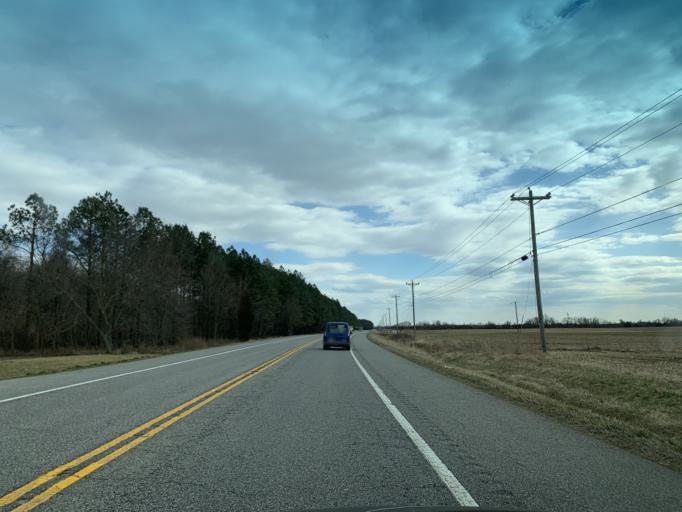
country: US
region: Maryland
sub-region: Queen Anne's County
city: Centreville
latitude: 38.9868
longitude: -76.0726
